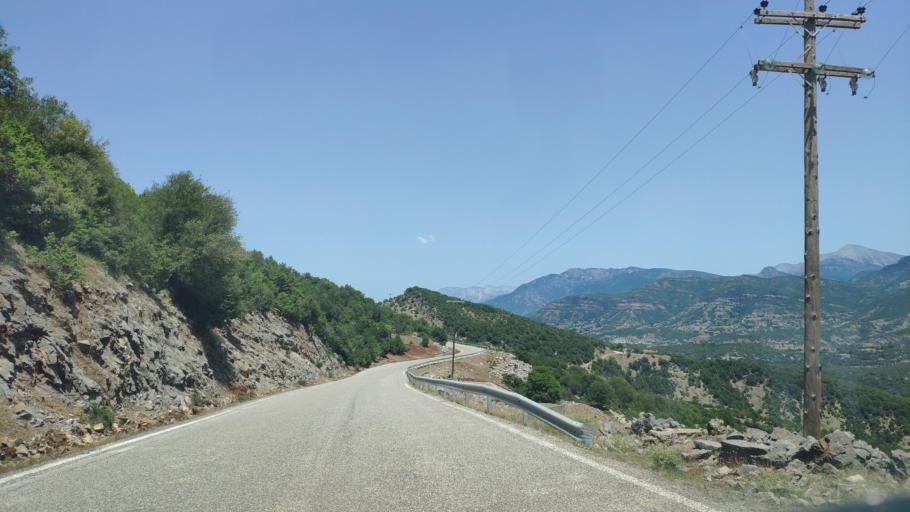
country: GR
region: Central Greece
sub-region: Nomos Evrytanias
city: Kerasochori
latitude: 39.0977
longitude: 21.4124
